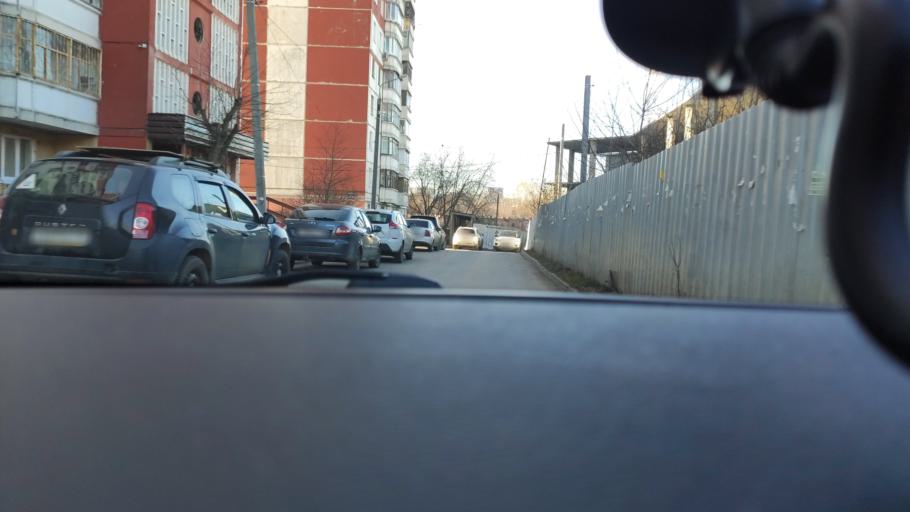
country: RU
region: Perm
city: Perm
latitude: 58.0066
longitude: 56.3007
